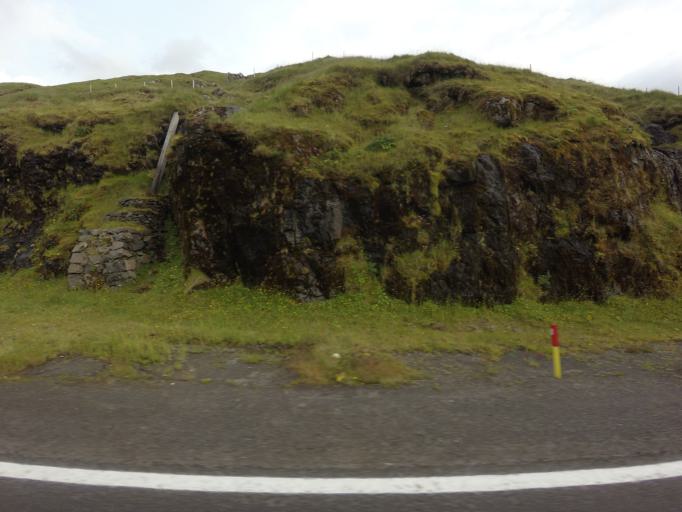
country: FO
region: Streymoy
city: Kollafjordhur
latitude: 62.1500
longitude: -6.9325
